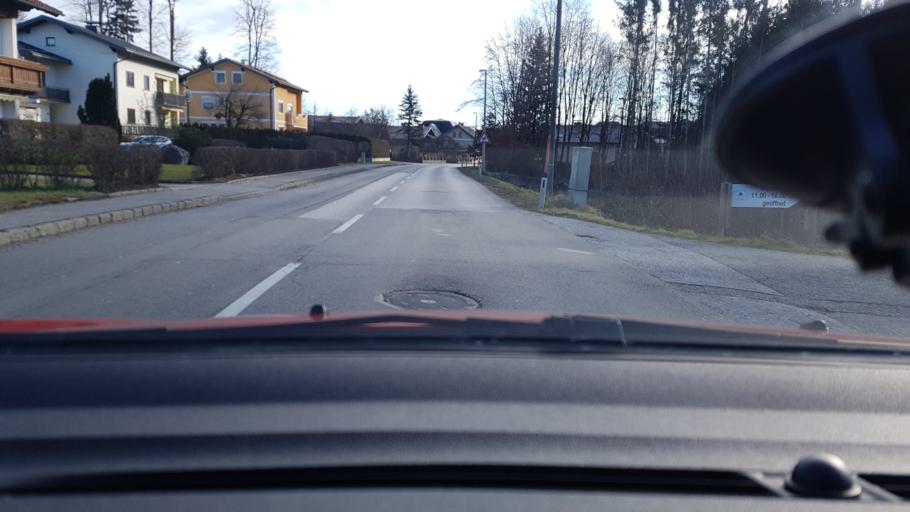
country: AT
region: Salzburg
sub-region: Politischer Bezirk Salzburg-Umgebung
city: Dorfbeuern
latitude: 48.0493
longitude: 12.9870
